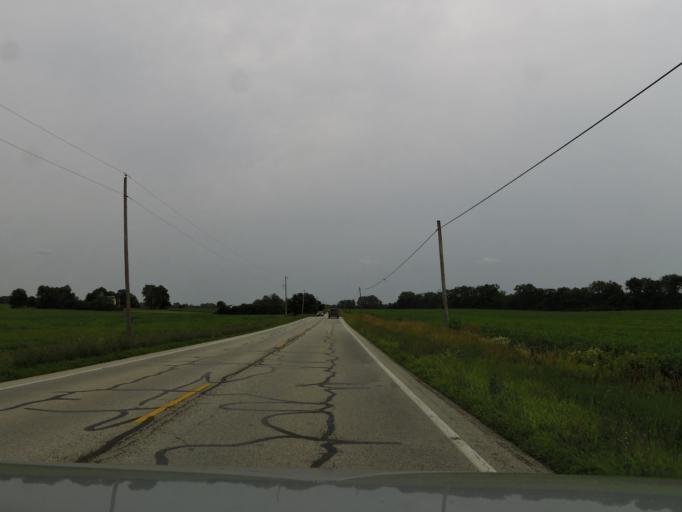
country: US
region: Ohio
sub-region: Warren County
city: Waynesville
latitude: 39.4956
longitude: -83.9773
